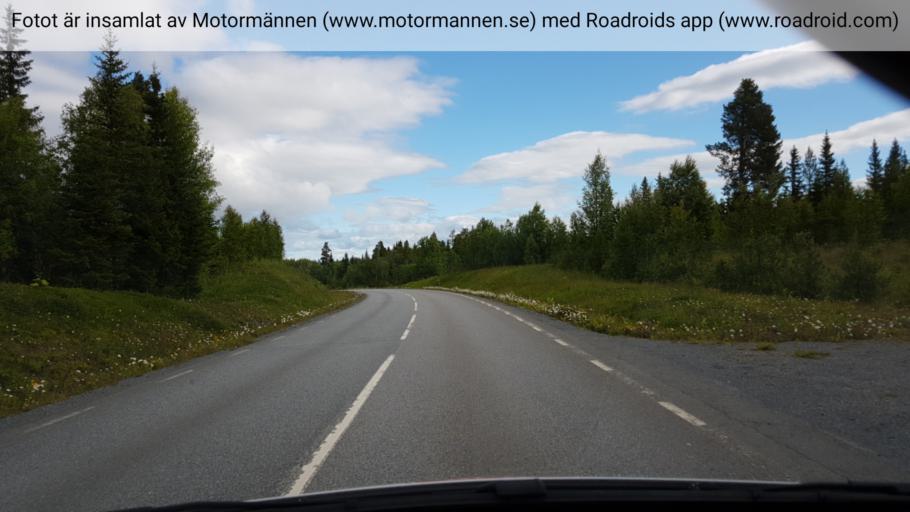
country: SE
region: Jaemtland
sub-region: Krokoms Kommun
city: Krokom
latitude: 63.2679
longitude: 14.4367
